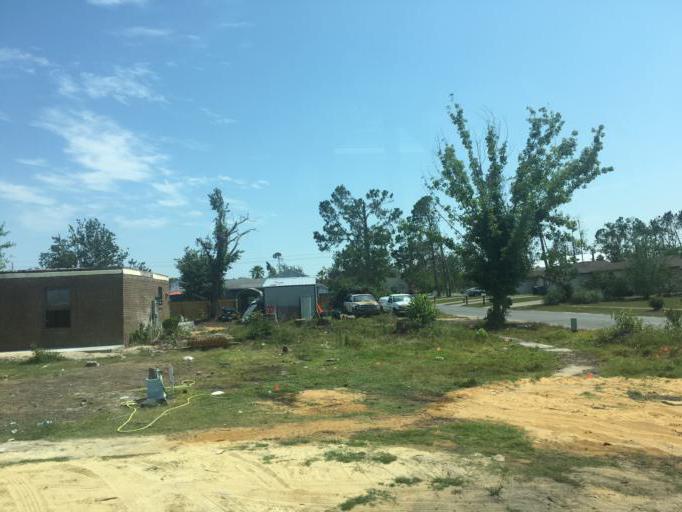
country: US
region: Florida
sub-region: Bay County
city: Lynn Haven
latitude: 30.2197
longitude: -85.6567
